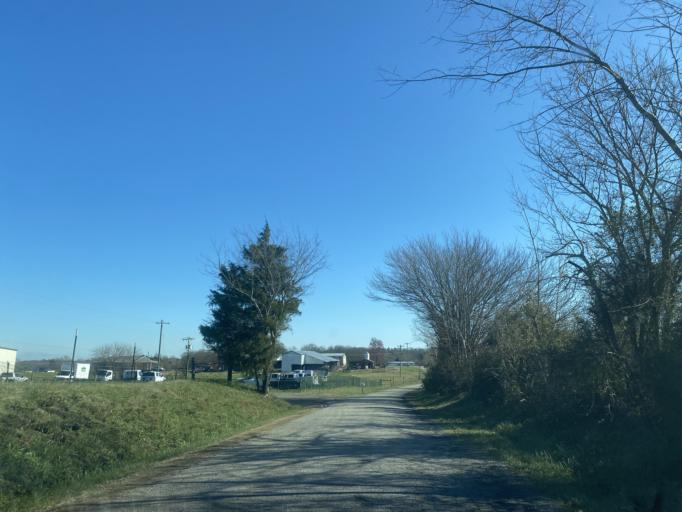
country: US
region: South Carolina
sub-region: Spartanburg County
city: Mayo
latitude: 35.1326
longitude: -81.7917
